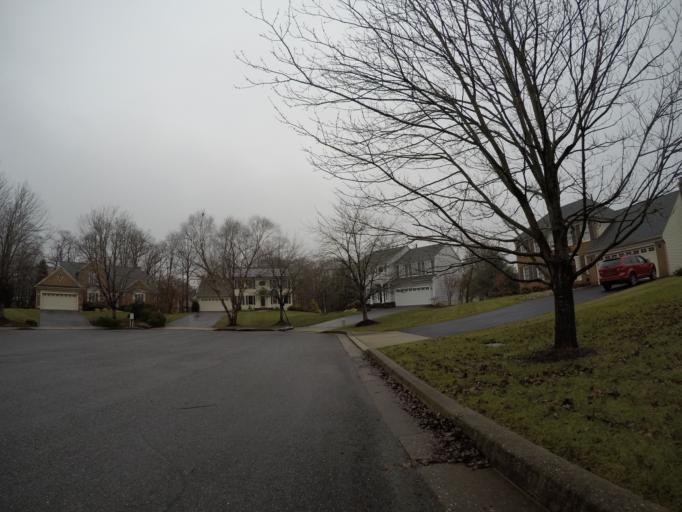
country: US
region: Maryland
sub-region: Howard County
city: Ellicott City
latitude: 39.2305
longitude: -76.7973
